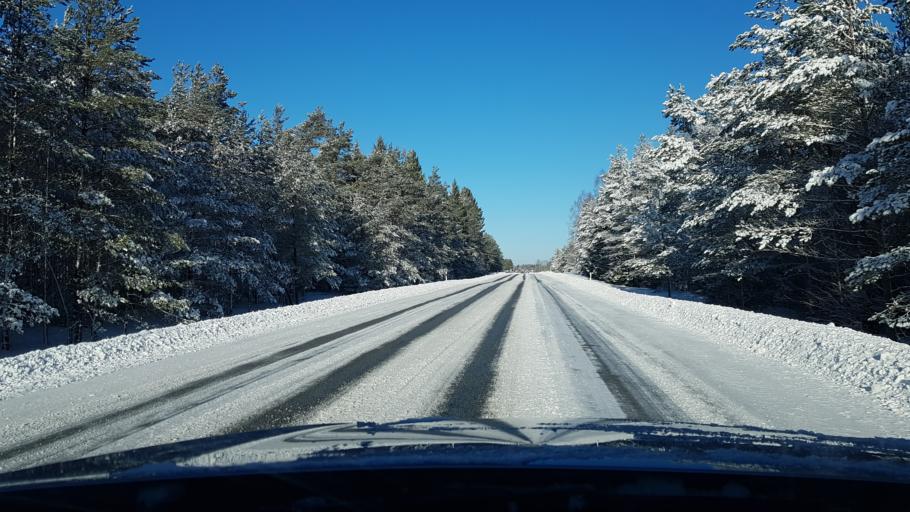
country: EE
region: Hiiumaa
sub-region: Kaerdla linn
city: Kardla
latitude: 58.9494
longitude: 22.7718
